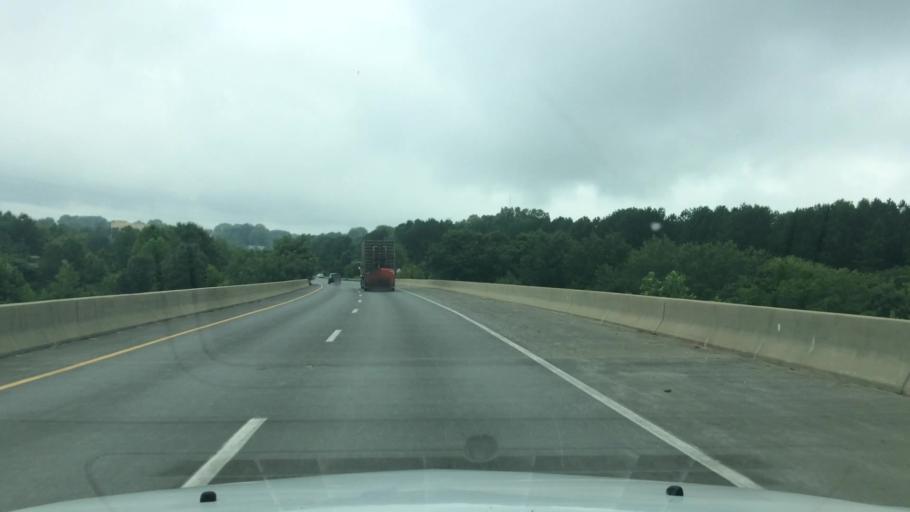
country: US
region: North Carolina
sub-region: Forsyth County
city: Clemmons
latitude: 36.0726
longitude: -80.3257
